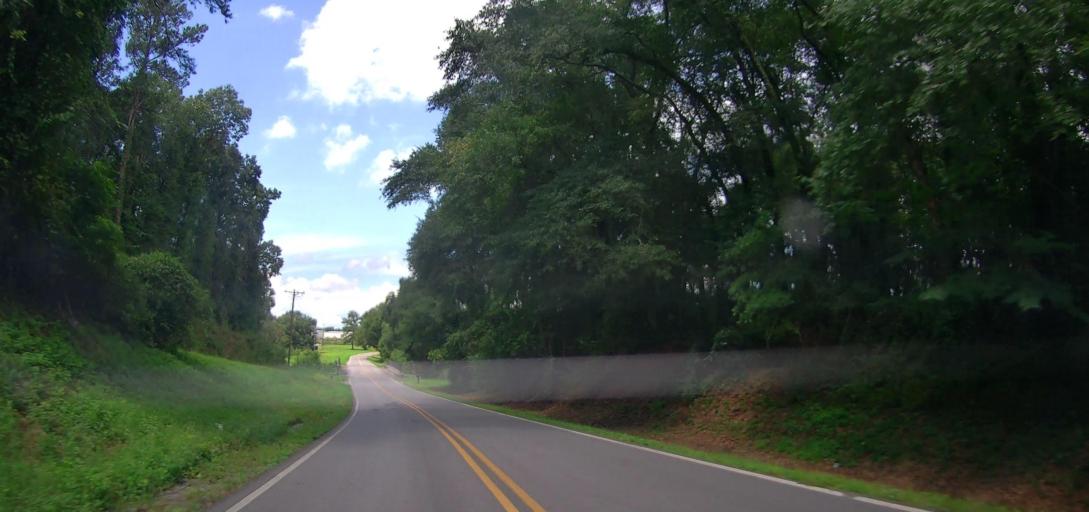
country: US
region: Georgia
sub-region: Houston County
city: Perry
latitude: 32.5199
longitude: -83.7199
